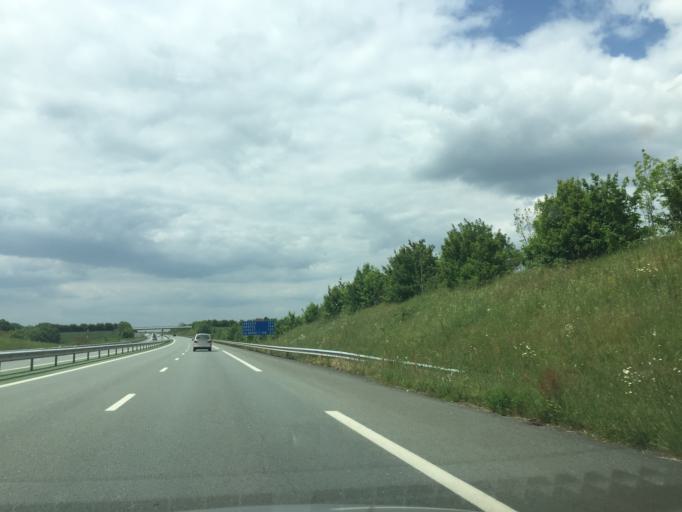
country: FR
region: Poitou-Charentes
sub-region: Departement des Deux-Sevres
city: Echire
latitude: 46.4196
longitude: -0.4123
